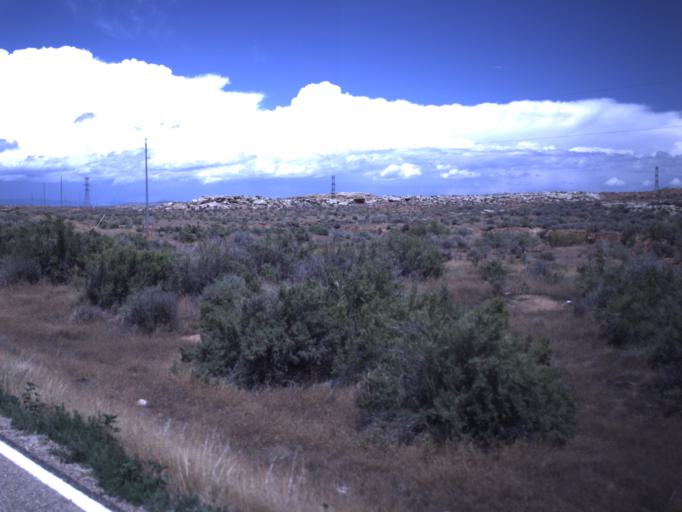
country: US
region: Utah
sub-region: Uintah County
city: Maeser
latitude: 40.2617
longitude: -109.6849
